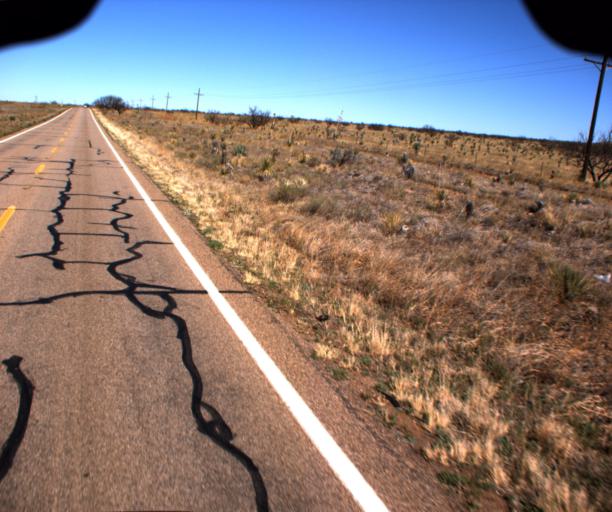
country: US
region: Arizona
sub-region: Cochise County
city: Huachuca City
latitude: 31.7143
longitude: -110.4621
